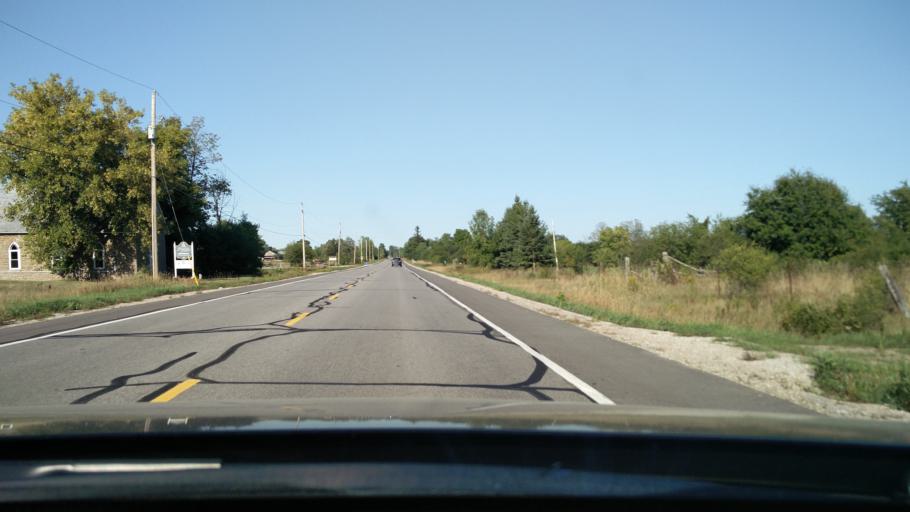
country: CA
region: Ontario
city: Perth
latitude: 44.9543
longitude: -76.1634
